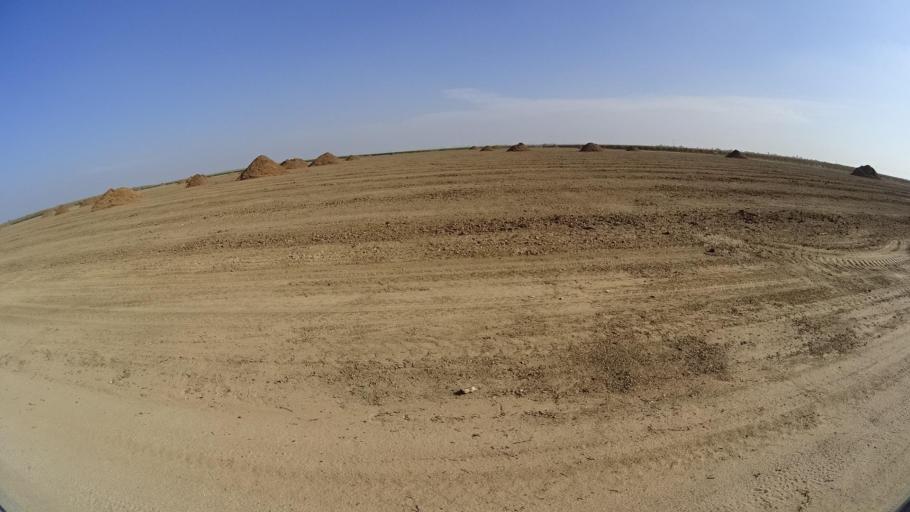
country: US
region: California
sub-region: Kern County
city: Shafter
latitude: 35.5348
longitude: -119.1336
